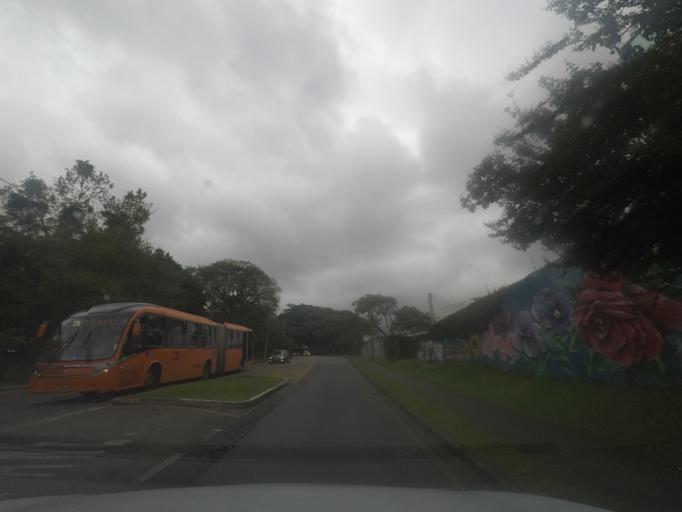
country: BR
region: Parana
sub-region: Curitiba
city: Curitiba
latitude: -25.4421
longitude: -49.2417
